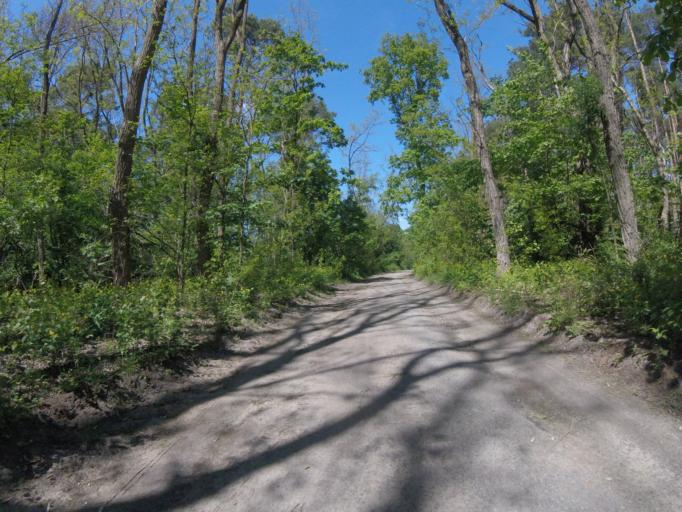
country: DE
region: Brandenburg
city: Teupitz
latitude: 52.1214
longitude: 13.5961
